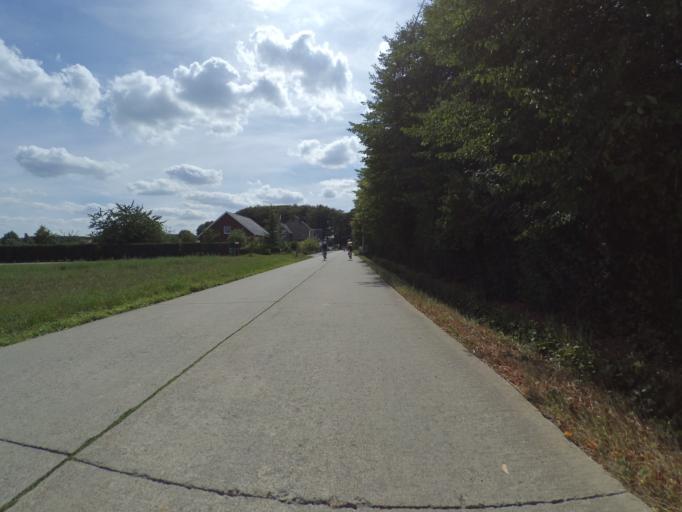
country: BE
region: Flanders
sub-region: Provincie Oost-Vlaanderen
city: Ronse
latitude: 50.7785
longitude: 3.6380
